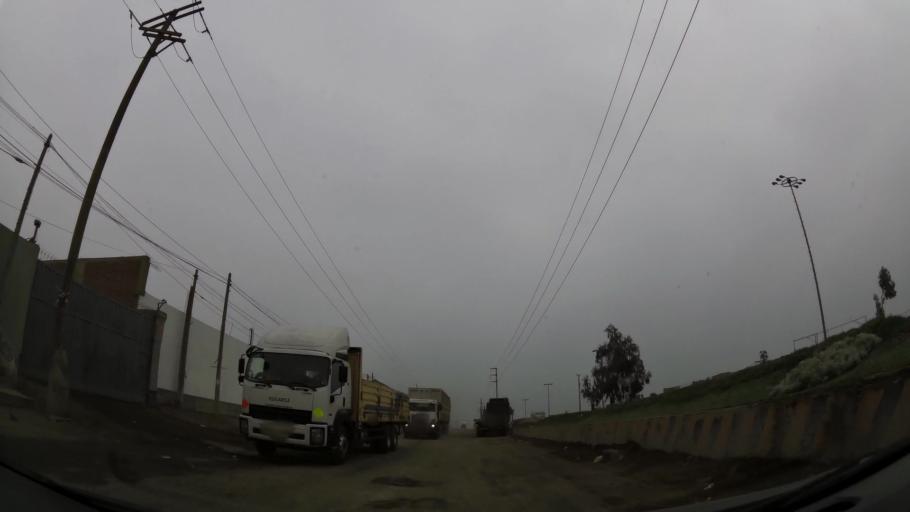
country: PE
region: Lima
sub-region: Lima
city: Surco
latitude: -12.2104
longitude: -76.9754
